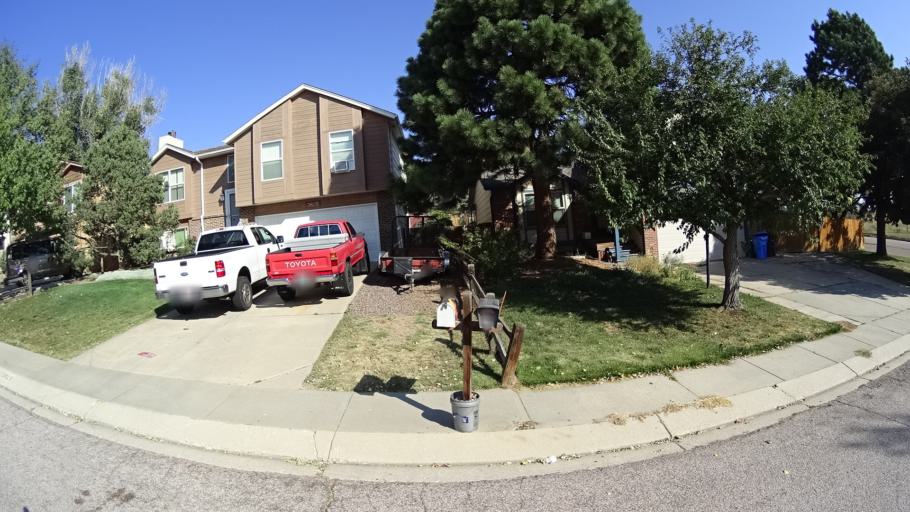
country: US
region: Colorado
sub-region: El Paso County
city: Cimarron Hills
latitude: 38.8879
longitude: -104.7230
